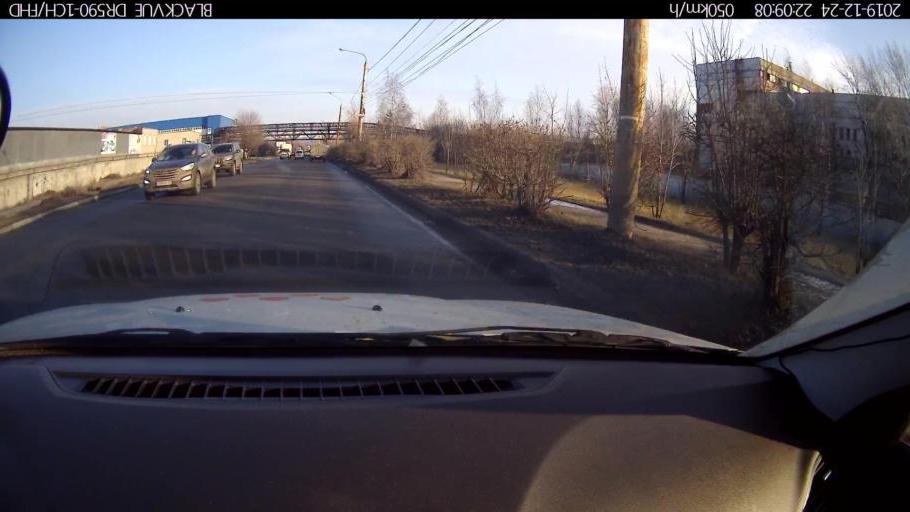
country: RU
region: Nizjnij Novgorod
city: Nizhniy Novgorod
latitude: 56.2522
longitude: 43.9201
